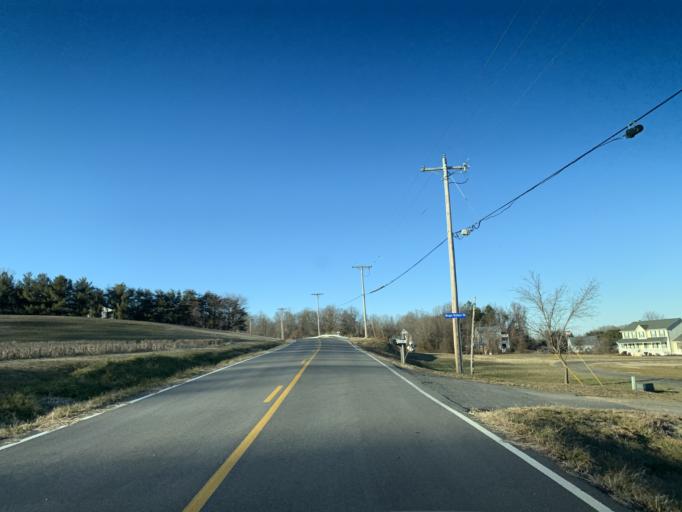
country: US
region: Maryland
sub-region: Saint Mary's County
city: Golden Beach
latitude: 38.4546
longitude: -76.6806
